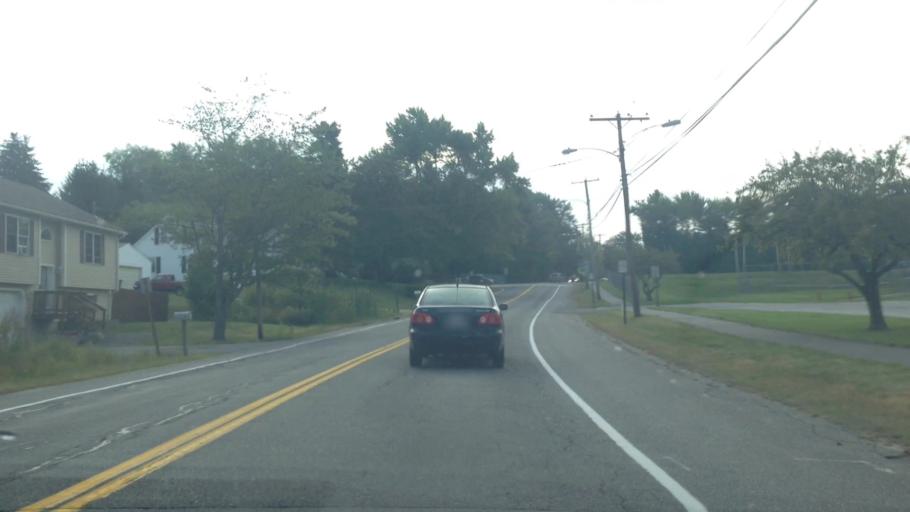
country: US
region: Maine
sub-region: Cumberland County
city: Westbrook
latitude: 43.6731
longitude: -70.3518
